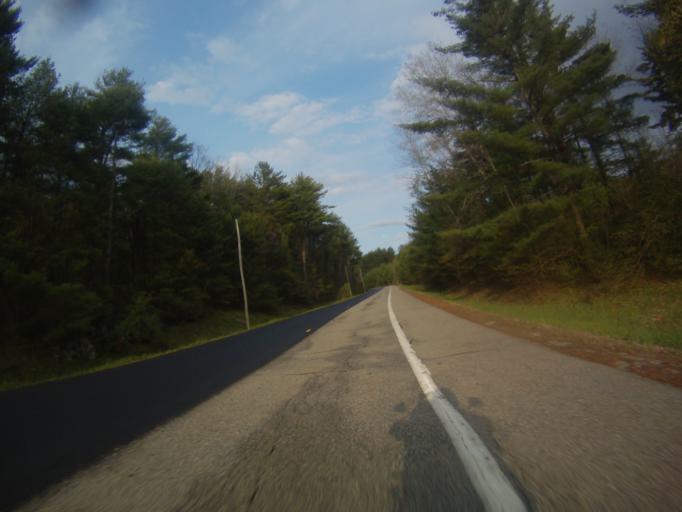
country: US
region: New York
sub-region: Essex County
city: Ticonderoga
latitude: 43.7437
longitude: -73.6432
